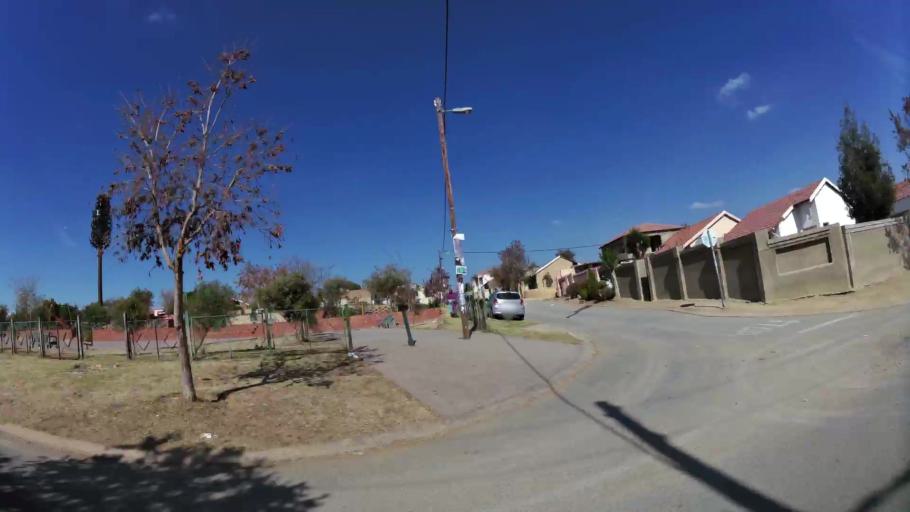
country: ZA
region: Gauteng
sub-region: West Rand District Municipality
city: Muldersdriseloop
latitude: -26.0157
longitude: 27.9348
